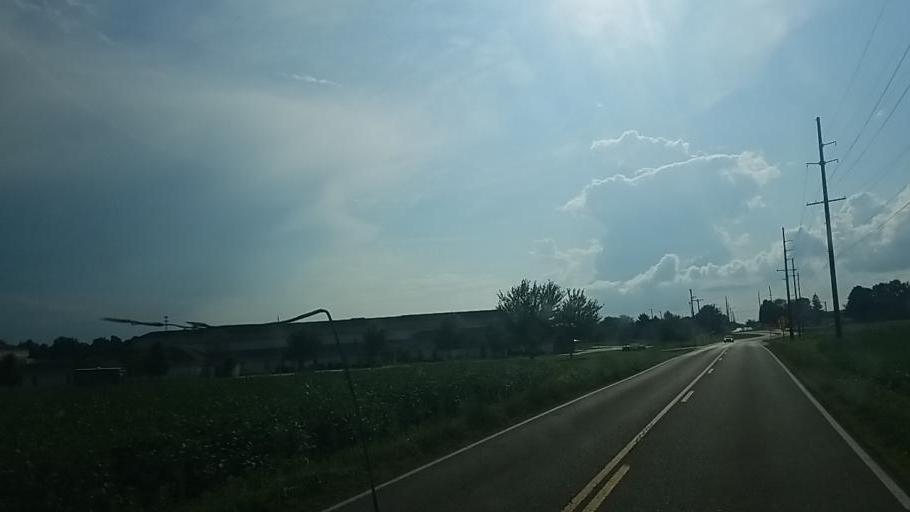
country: US
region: Ohio
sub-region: Wayne County
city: Wooster
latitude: 40.8579
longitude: -81.9471
